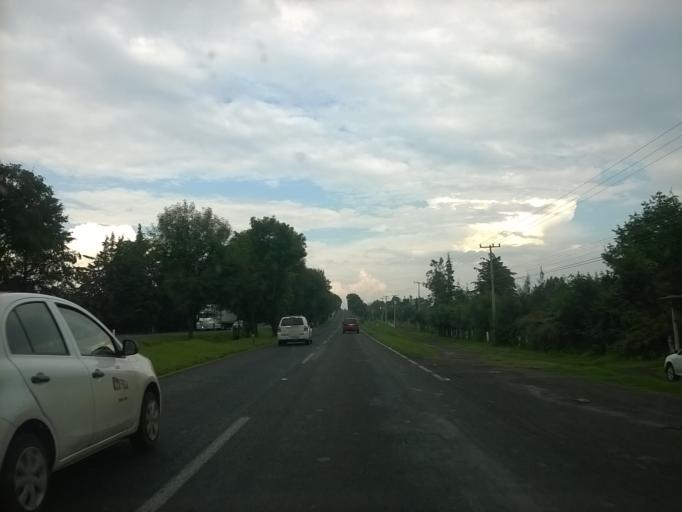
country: MX
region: Michoacan
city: Cuanajo
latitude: 19.5354
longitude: -101.5118
